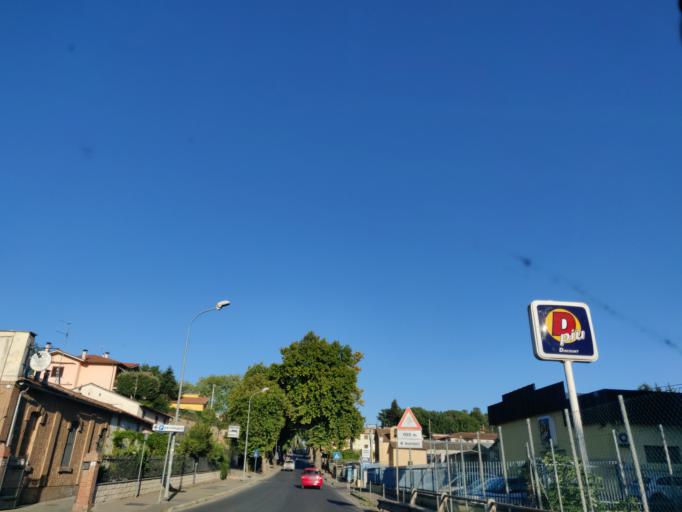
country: IT
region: Latium
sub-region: Provincia di Viterbo
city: Acquapendente
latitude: 42.7422
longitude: 11.8718
